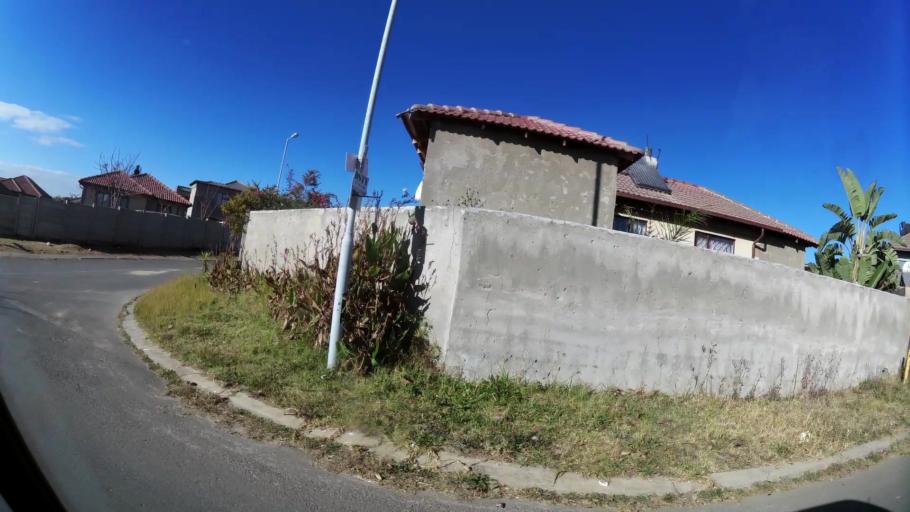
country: ZA
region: Gauteng
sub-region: City of Tshwane Metropolitan Municipality
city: Centurion
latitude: -25.8944
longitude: 28.1007
